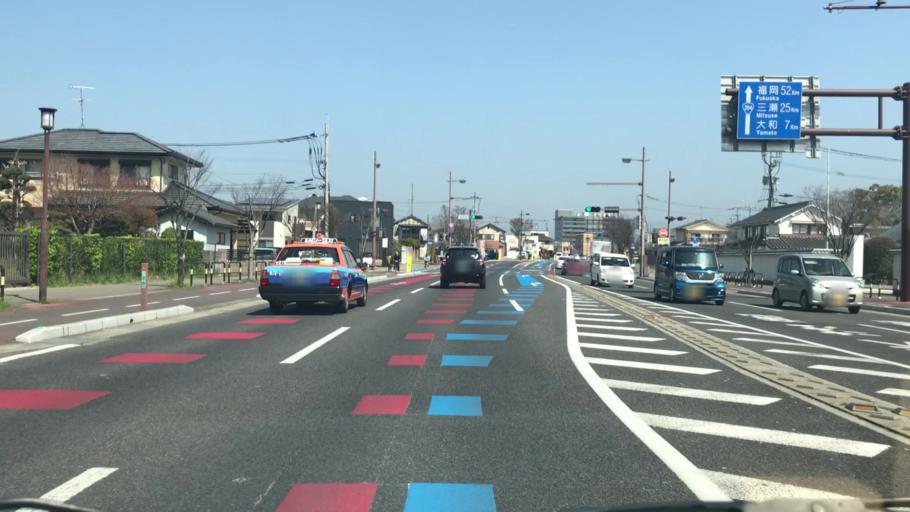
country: JP
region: Saga Prefecture
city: Saga-shi
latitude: 33.2512
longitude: 130.2922
